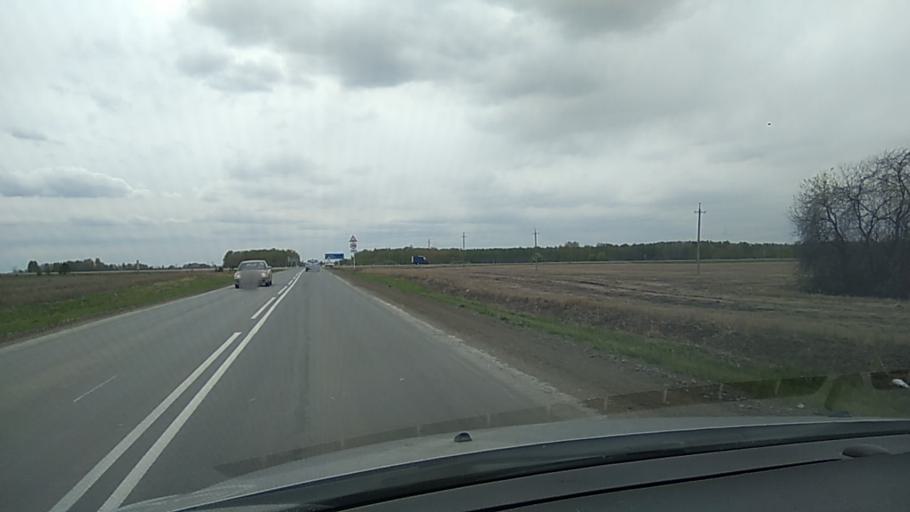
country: RU
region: Sverdlovsk
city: Martyush
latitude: 56.4109
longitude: 61.7902
